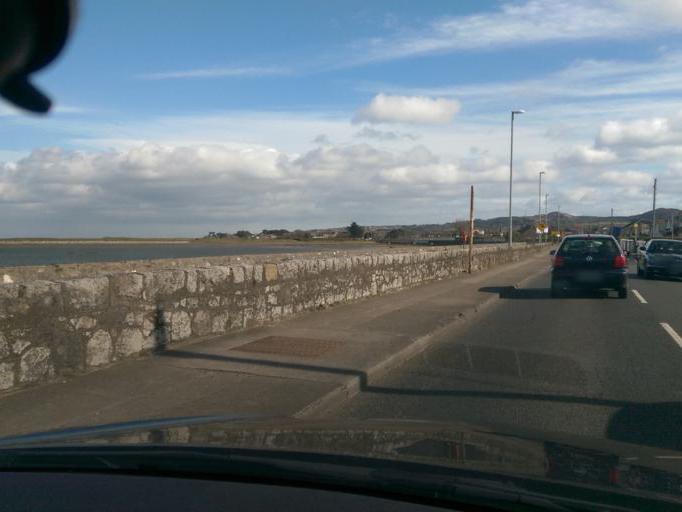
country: IE
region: Leinster
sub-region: Fingal County
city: Baldoyle
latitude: 53.3938
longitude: -6.1212
